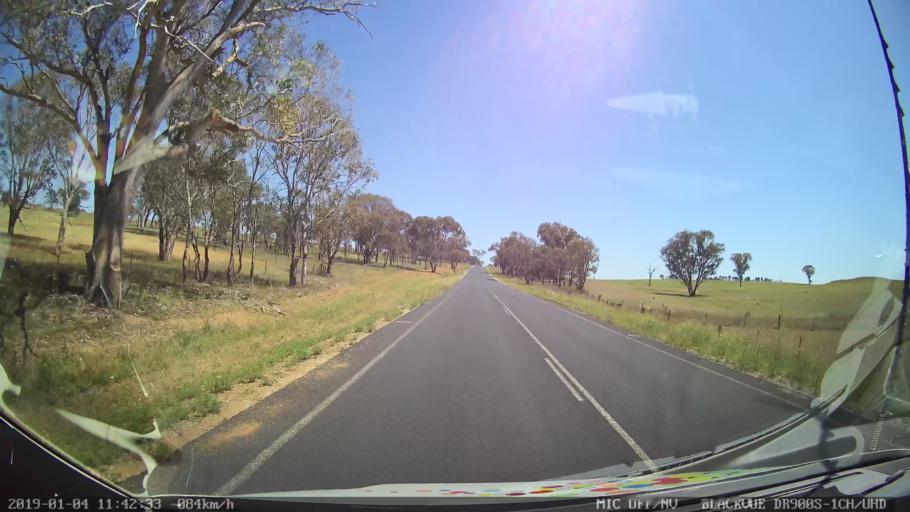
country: AU
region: New South Wales
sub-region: Cabonne
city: Molong
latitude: -32.9803
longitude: 148.7864
